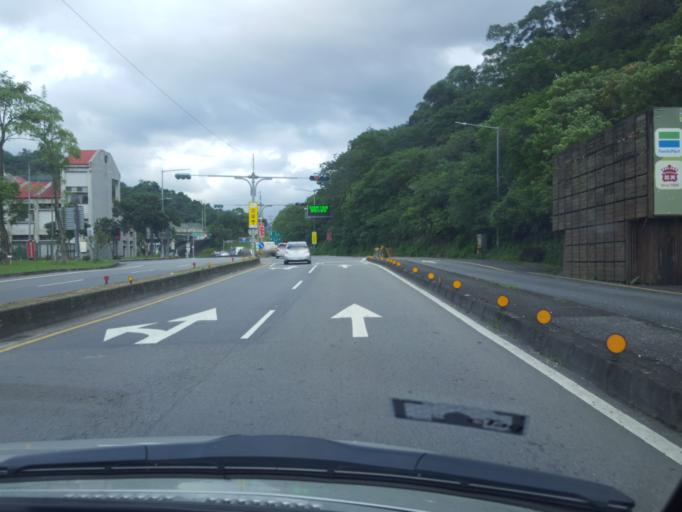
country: TW
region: Taipei
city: Taipei
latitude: 25.0085
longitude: 121.6453
